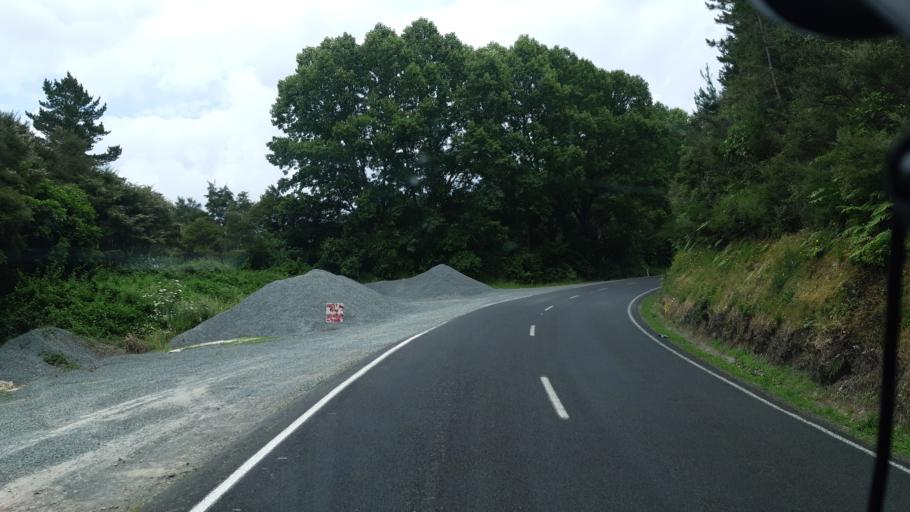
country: NZ
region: Waikato
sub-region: South Waikato District
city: Tokoroa
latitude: -38.2738
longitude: 175.6696
